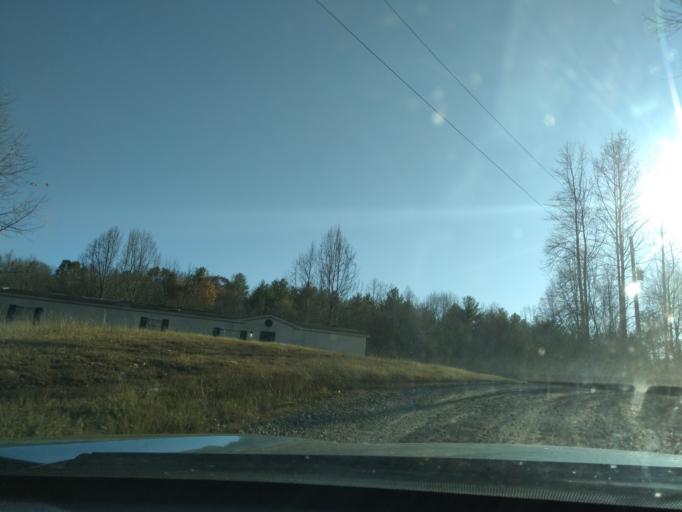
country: US
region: Virginia
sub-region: Floyd County
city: Floyd
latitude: 36.8383
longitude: -80.1915
